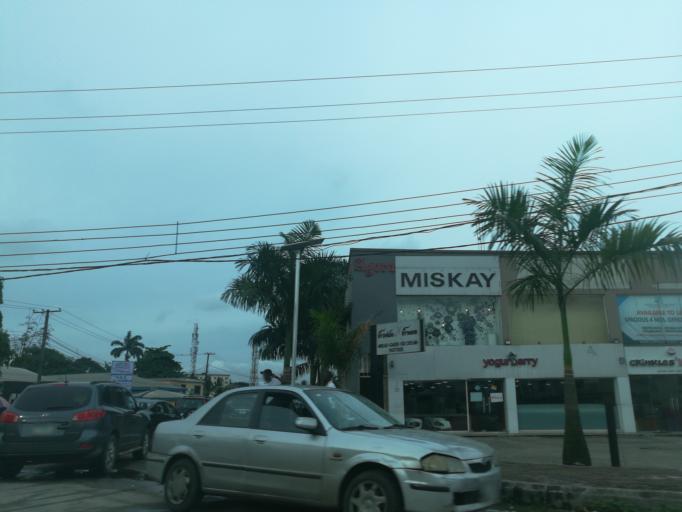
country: NG
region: Rivers
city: Port Harcourt
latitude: 4.8128
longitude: 6.9979
